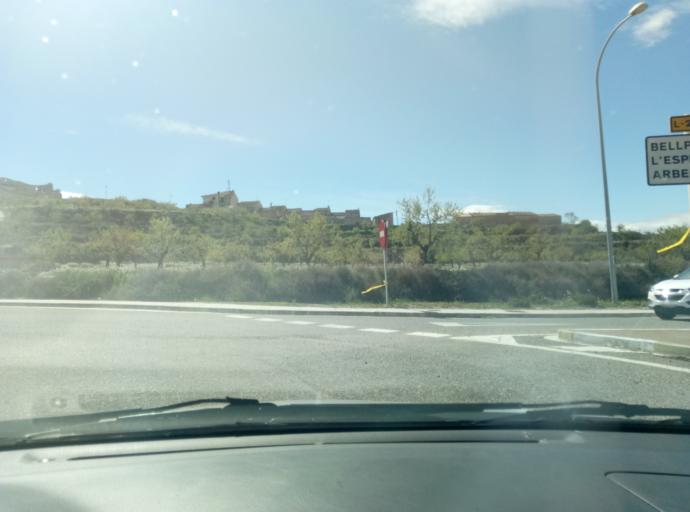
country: ES
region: Catalonia
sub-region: Provincia de Lleida
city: Vallbona de les Monges
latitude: 41.5532
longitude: 1.0360
